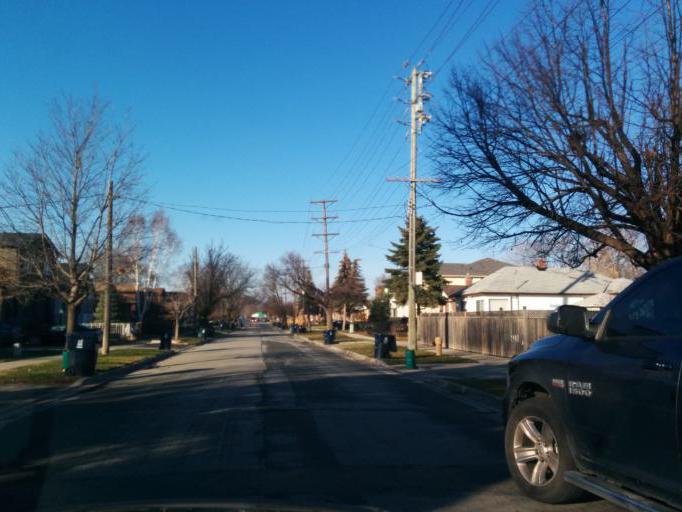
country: CA
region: Ontario
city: Etobicoke
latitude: 43.6097
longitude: -79.5314
